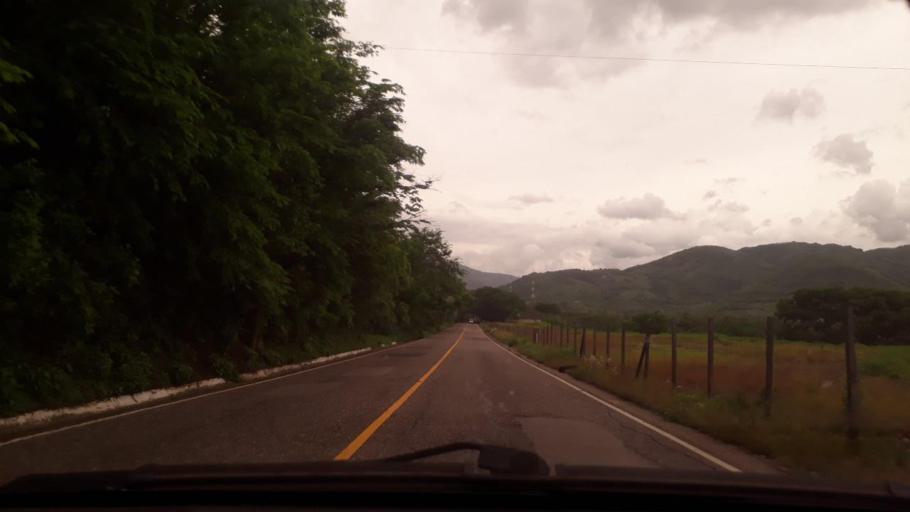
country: GT
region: Chiquimula
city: San Jose La Arada
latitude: 14.7409
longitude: -89.5554
